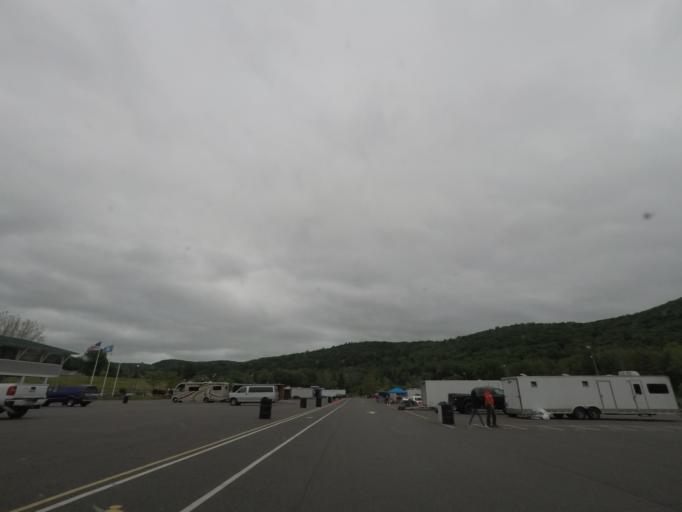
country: US
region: Connecticut
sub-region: Litchfield County
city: Canaan
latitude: 41.9280
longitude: -73.3818
